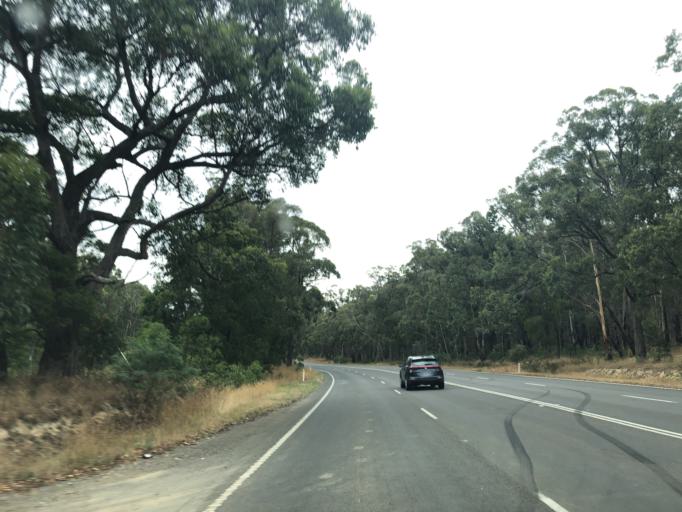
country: AU
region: Victoria
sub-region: Hume
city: Sunbury
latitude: -37.3916
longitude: 144.5270
